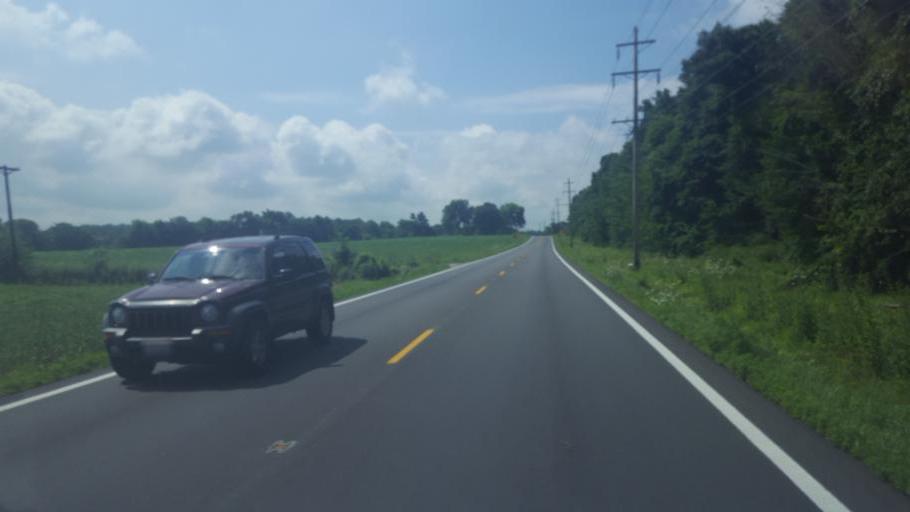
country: US
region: Ohio
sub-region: Fairfield County
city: Baltimore
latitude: 39.8156
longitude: -82.5705
